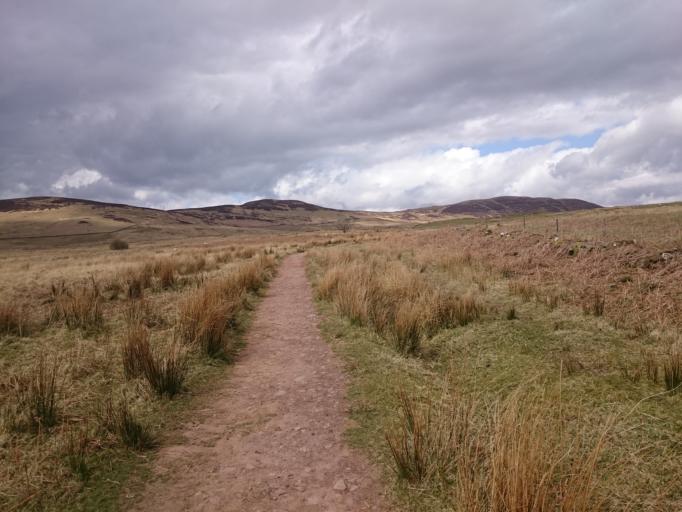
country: GB
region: Scotland
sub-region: West Dunbartonshire
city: Balloch
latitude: 56.0962
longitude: -4.4914
